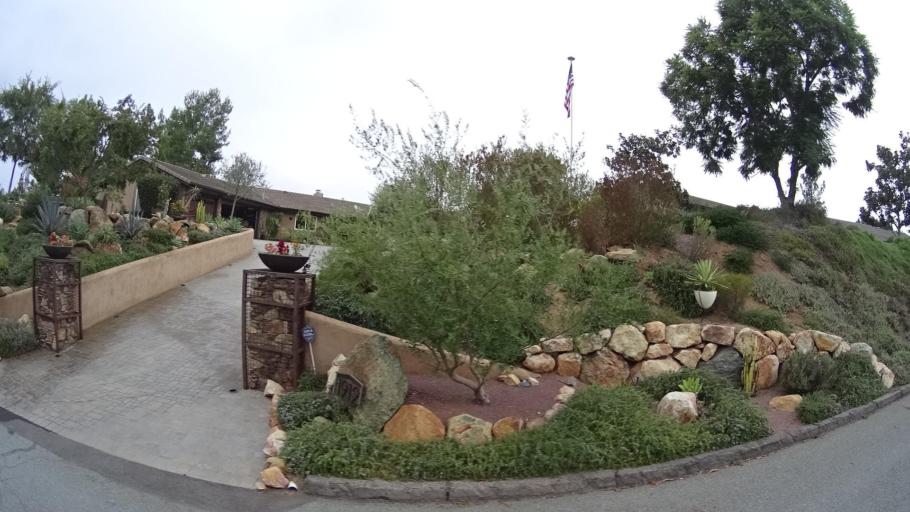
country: US
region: California
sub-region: San Diego County
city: Granite Hills
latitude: 32.7750
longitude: -116.9157
